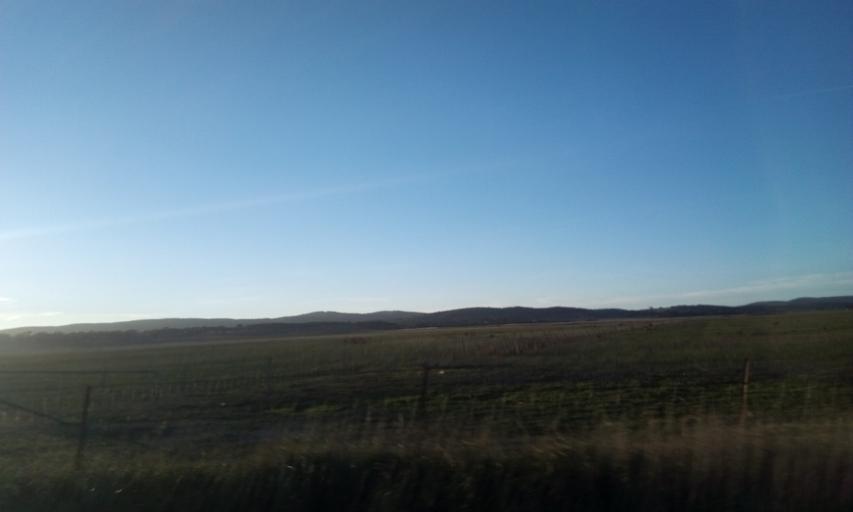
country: AU
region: New South Wales
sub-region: Goulburn Mulwaree
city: Goulburn
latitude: -34.8475
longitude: 149.5569
